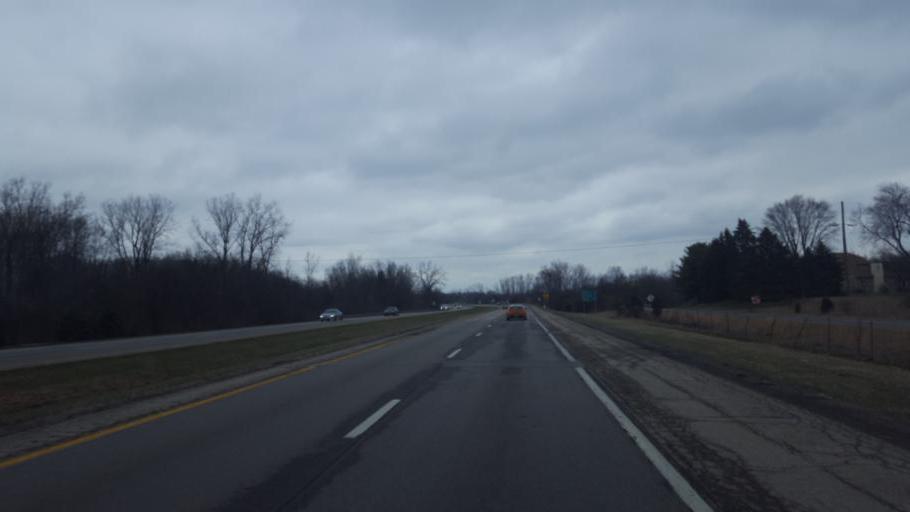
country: US
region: Ohio
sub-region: Marion County
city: Prospect
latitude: 40.4297
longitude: -83.0733
